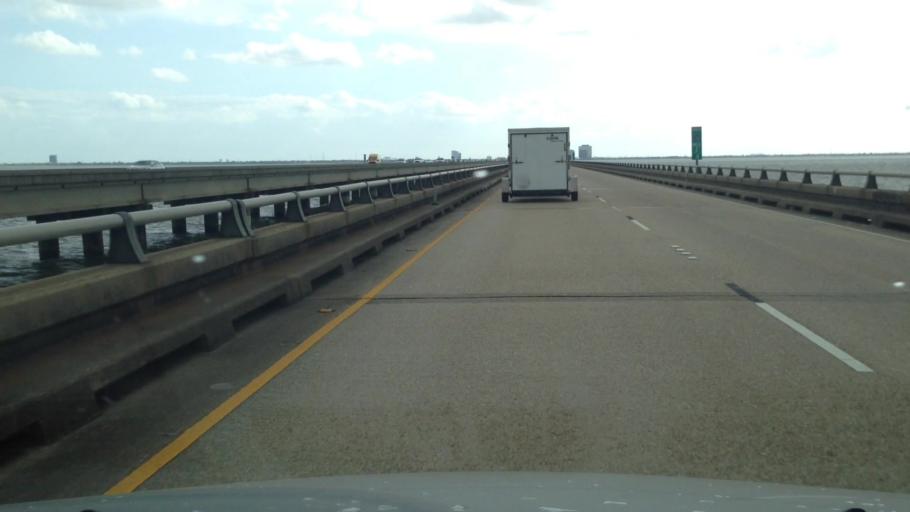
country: US
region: Louisiana
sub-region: Jefferson Parish
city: Metairie
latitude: 30.0622
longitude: -90.1470
